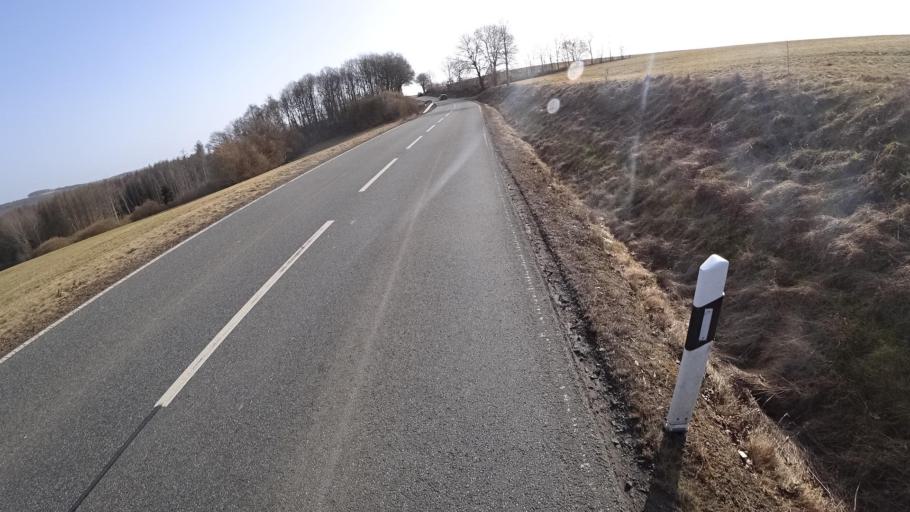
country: DE
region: Rheinland-Pfalz
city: Etzbach
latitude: 50.7741
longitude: 7.6963
